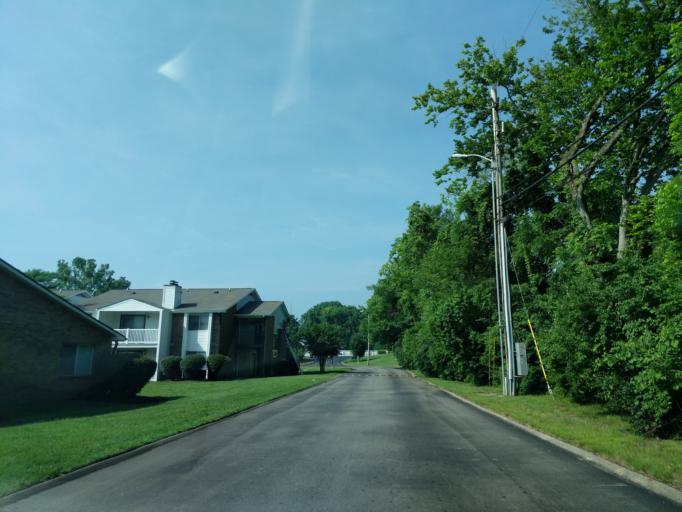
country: US
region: Tennessee
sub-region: Davidson County
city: Goodlettsville
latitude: 36.2993
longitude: -86.7100
